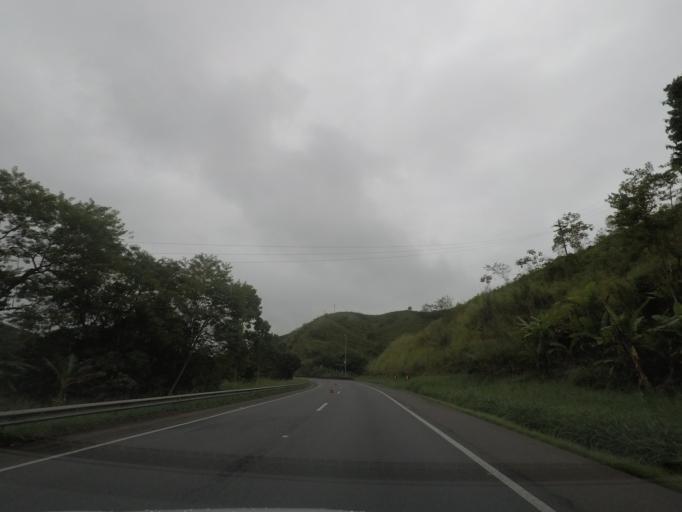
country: BR
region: Sao Paulo
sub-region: Cajati
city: Cajati
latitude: -24.8029
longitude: -48.2112
